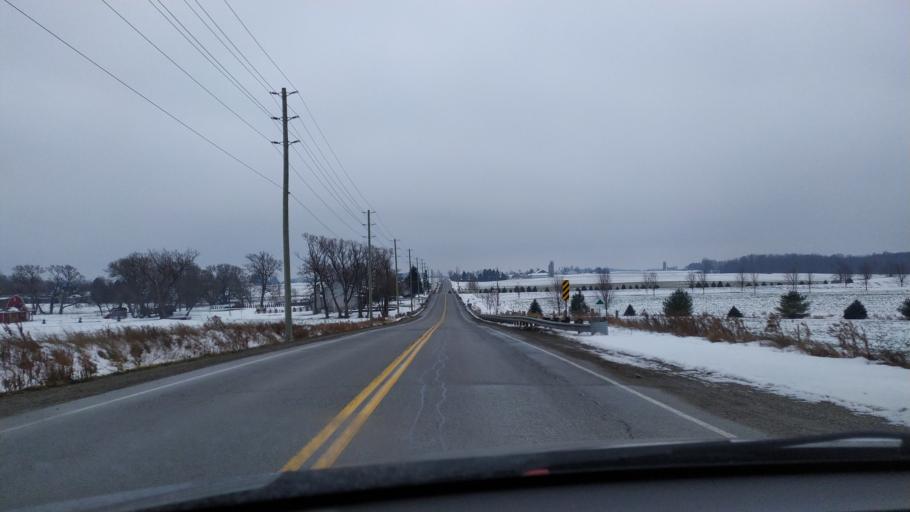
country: CA
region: Ontario
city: Waterloo
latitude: 43.5155
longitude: -80.6201
